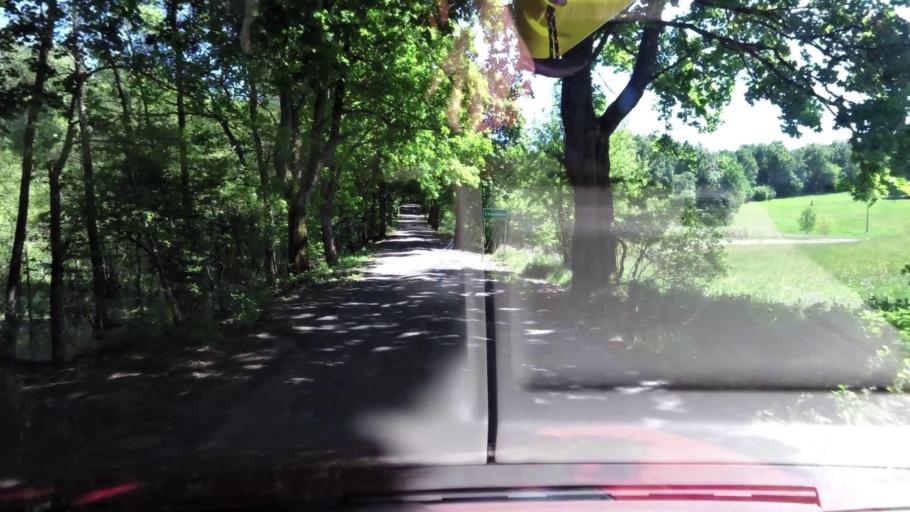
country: PL
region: West Pomeranian Voivodeship
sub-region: Powiat koszalinski
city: Polanow
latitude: 54.0383
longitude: 16.7681
